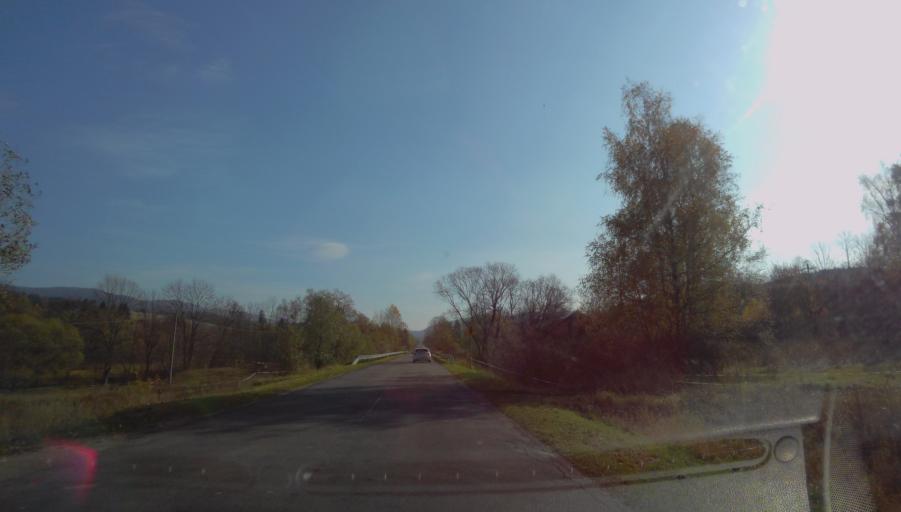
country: PL
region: Subcarpathian Voivodeship
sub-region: Powiat sanocki
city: Komancza
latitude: 49.2321
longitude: 22.1566
